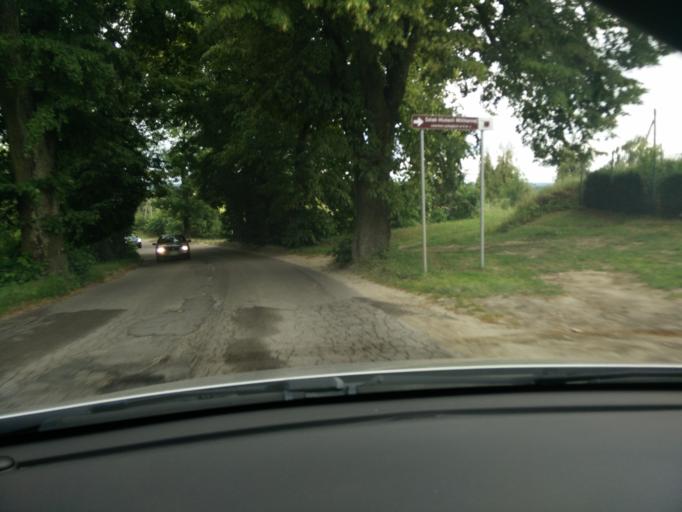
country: PL
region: Pomeranian Voivodeship
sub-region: Powiat pucki
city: Mrzezino
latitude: 54.6496
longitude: 18.4328
